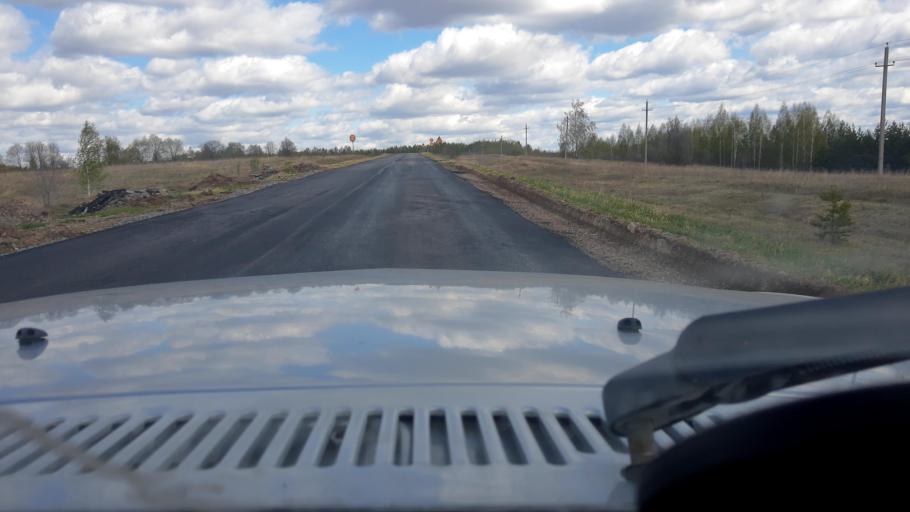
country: RU
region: Bashkortostan
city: Pavlovka
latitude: 55.3610
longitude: 56.4133
